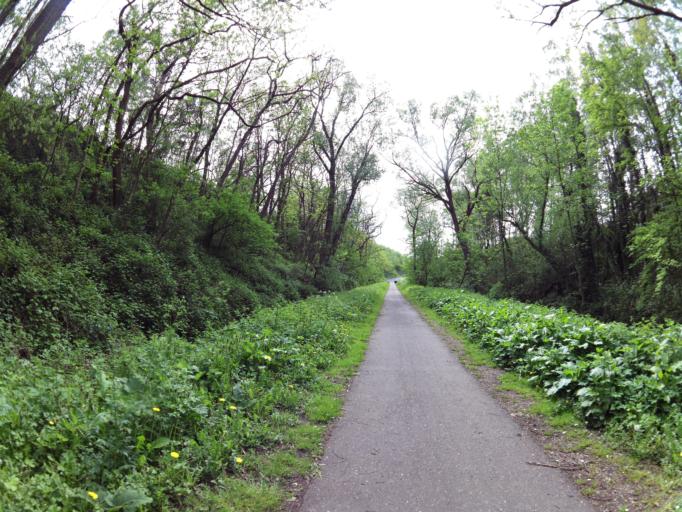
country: NL
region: Limburg
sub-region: Gemeente Kerkrade
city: Kerkrade
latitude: 50.8921
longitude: 6.0745
